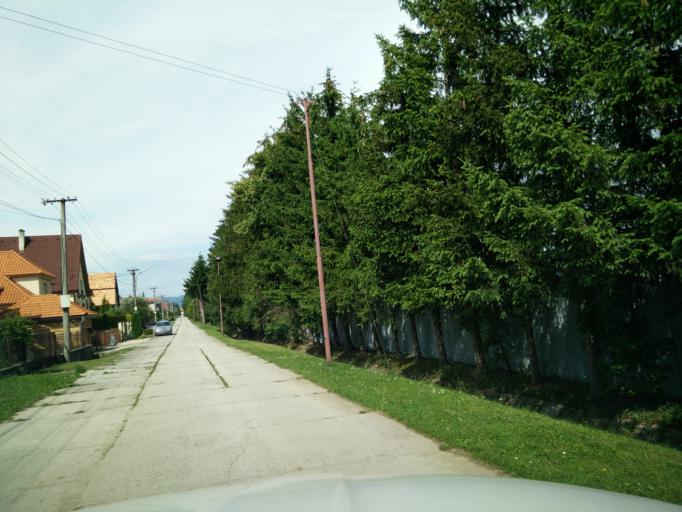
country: SK
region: Nitriansky
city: Prievidza
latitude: 48.8135
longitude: 18.6169
